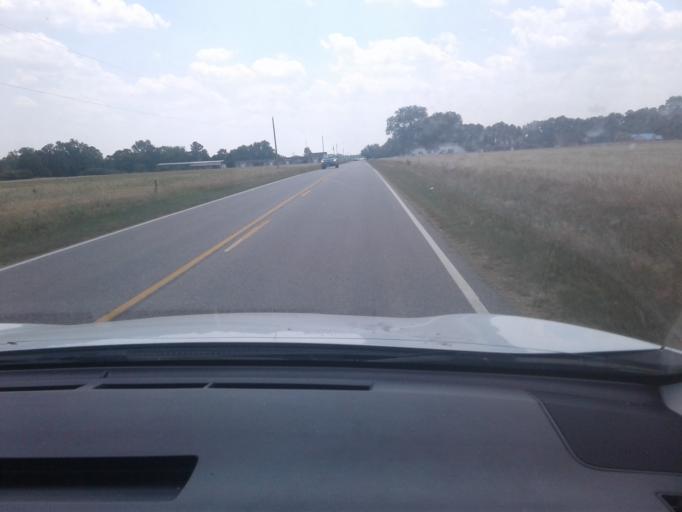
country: US
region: North Carolina
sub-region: Harnett County
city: Coats
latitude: 35.3684
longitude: -78.6316
